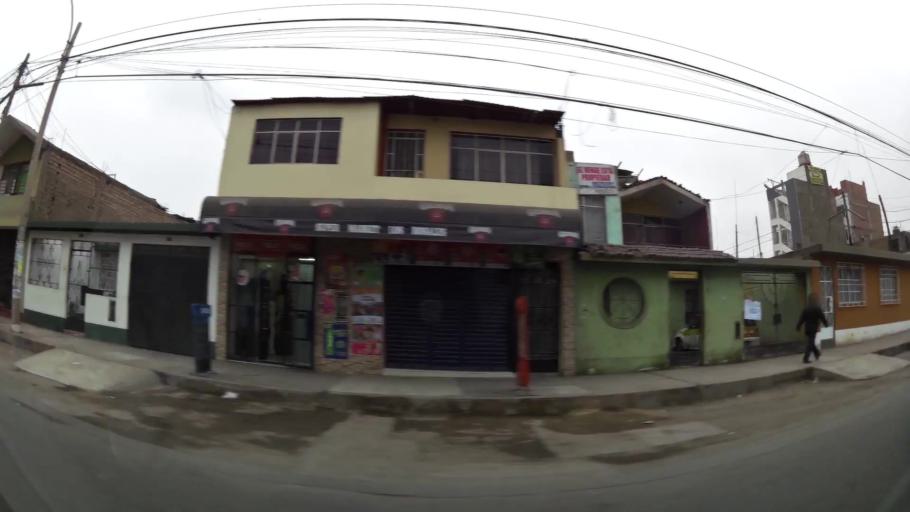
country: PE
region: Lima
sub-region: Lima
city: Independencia
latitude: -11.9320
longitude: -77.0579
